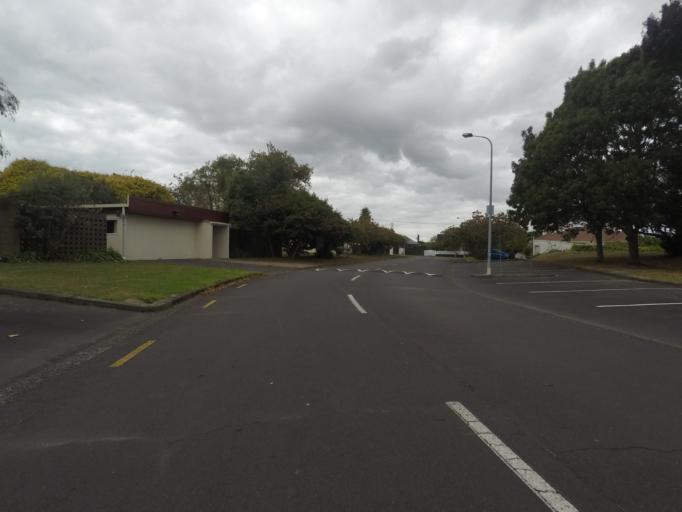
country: NZ
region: Auckland
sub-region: Auckland
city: Auckland
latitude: -36.8739
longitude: 174.7219
